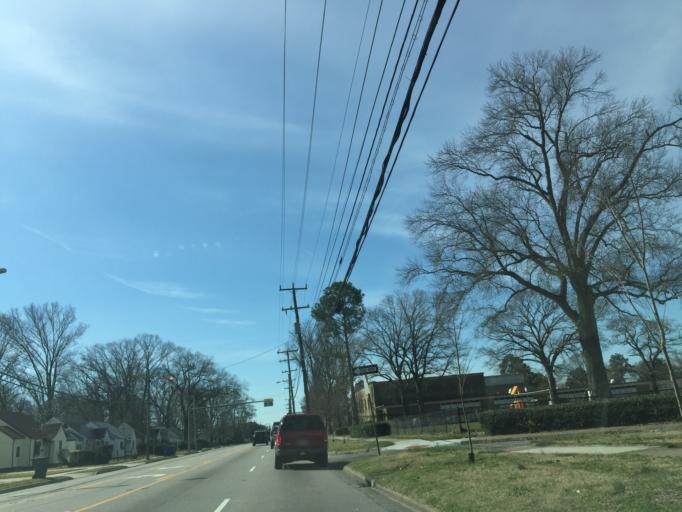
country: US
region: Virginia
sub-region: City of Norfolk
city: Norfolk
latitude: 36.8829
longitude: -76.2616
